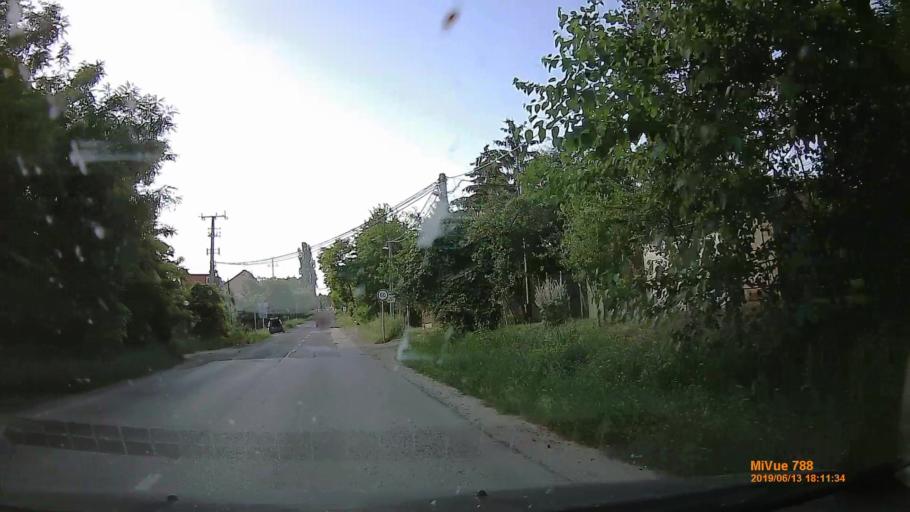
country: HU
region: Pest
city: Ecser
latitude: 47.4564
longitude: 19.3014
